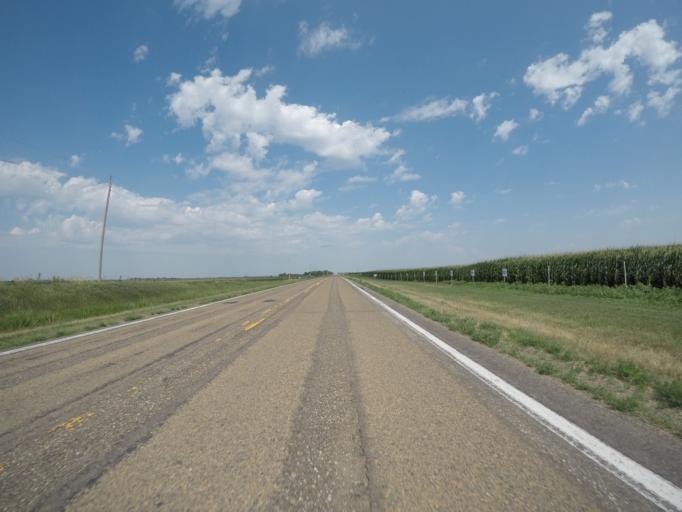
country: US
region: Nebraska
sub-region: Nuckolls County
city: Superior
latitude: 40.0166
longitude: -97.8618
